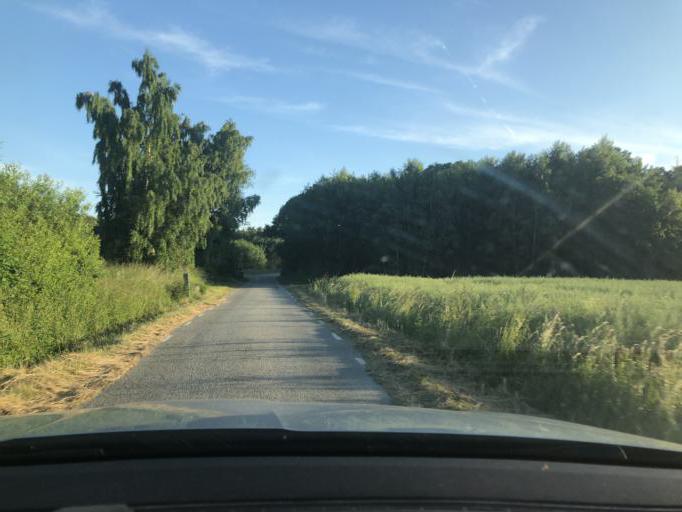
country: SE
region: Blekinge
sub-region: Solvesborgs Kommun
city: Soelvesborg
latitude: 56.1415
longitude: 14.6341
